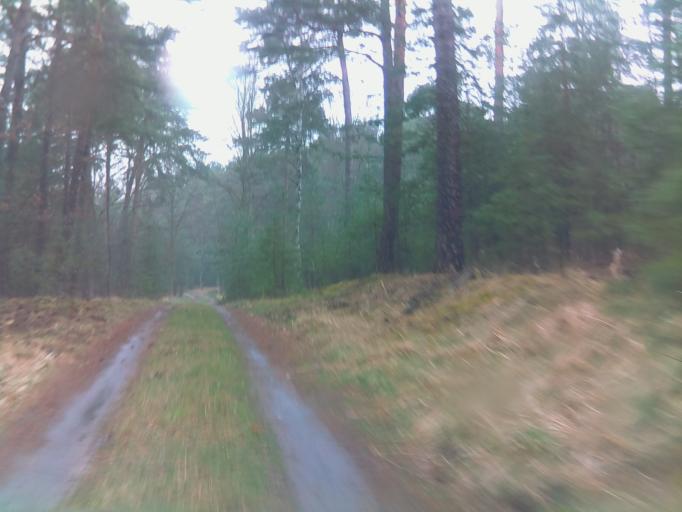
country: DE
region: Brandenburg
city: Jamlitz
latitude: 52.0047
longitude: 14.3847
